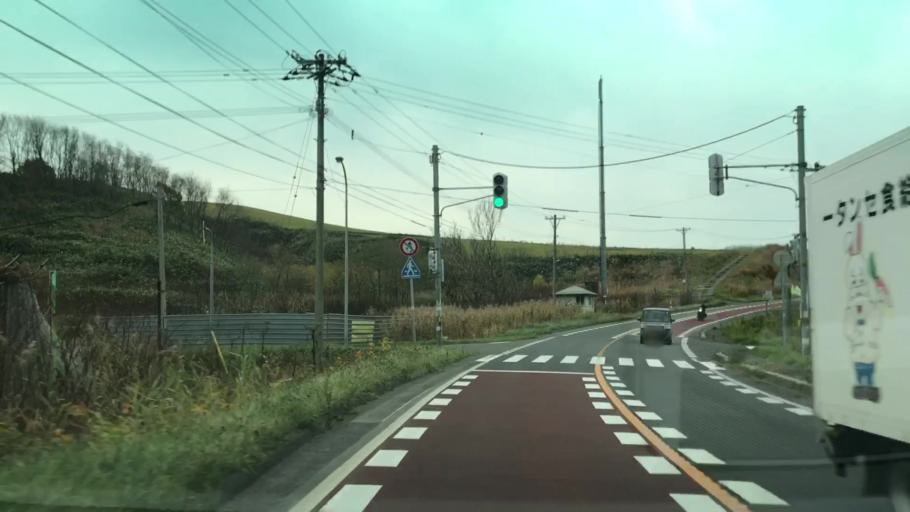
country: JP
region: Hokkaido
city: Ishikari
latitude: 43.3554
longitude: 141.4303
